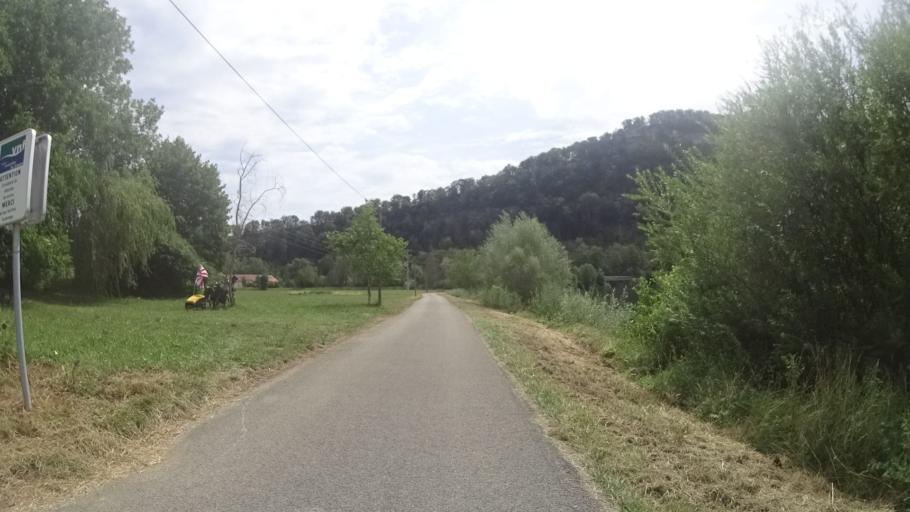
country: FR
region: Franche-Comte
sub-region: Departement du Doubs
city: Baume-les-Dames
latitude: 47.3443
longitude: 6.3738
